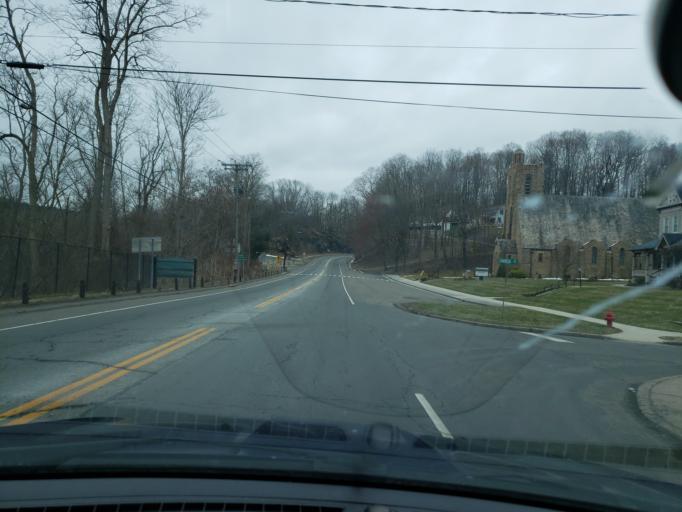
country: US
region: Connecticut
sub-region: Hartford County
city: Collinsville
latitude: 41.8095
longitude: -72.9261
